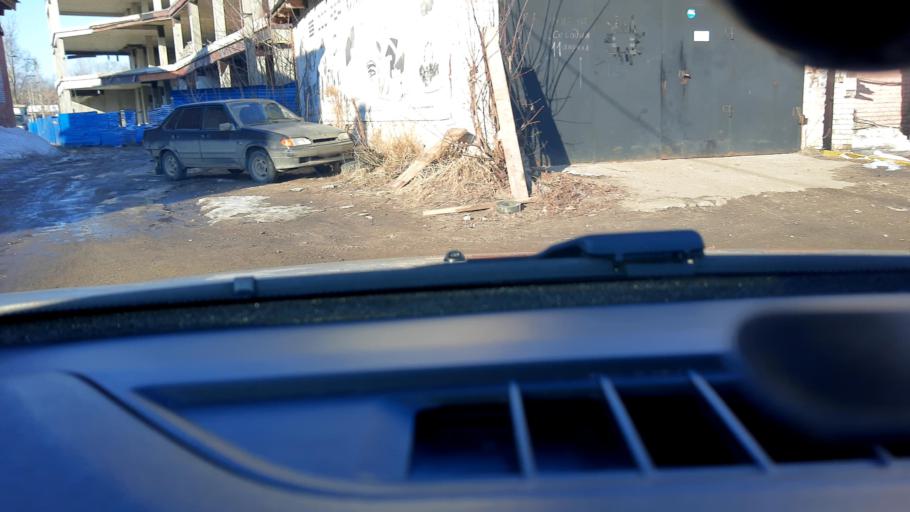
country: RU
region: Nizjnij Novgorod
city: Gorbatovka
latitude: 56.3607
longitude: 43.8297
